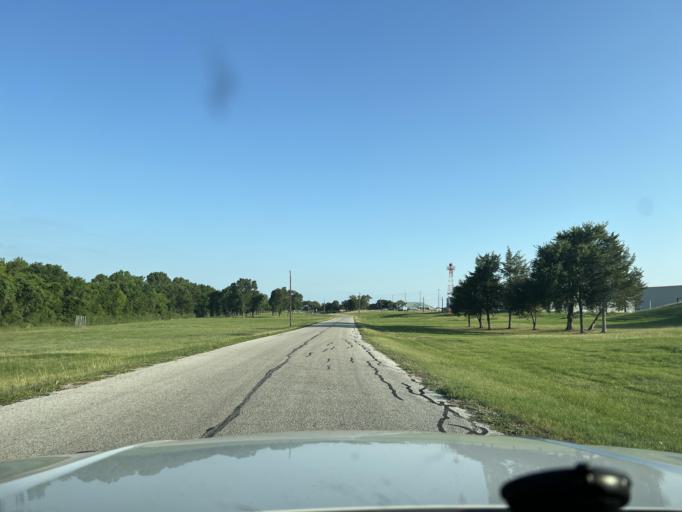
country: US
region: Texas
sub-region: Washington County
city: Brenham
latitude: 30.2204
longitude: -96.3718
